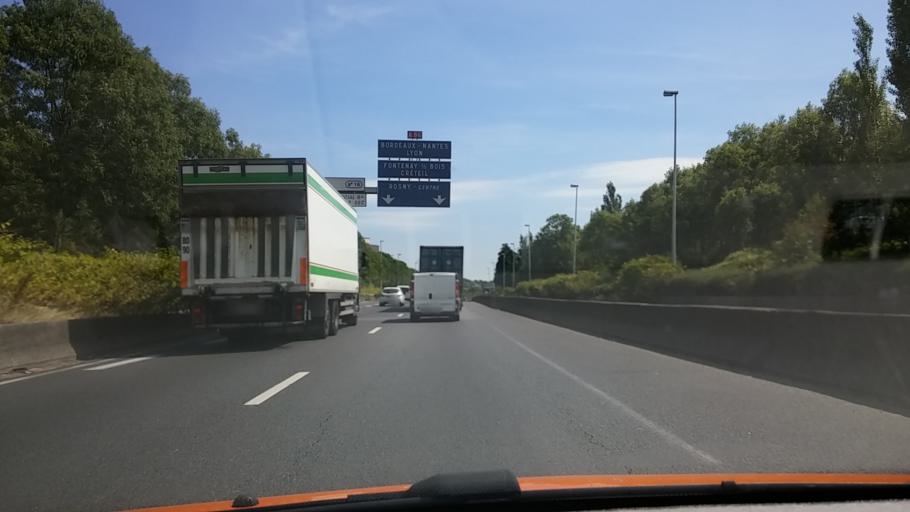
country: FR
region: Ile-de-France
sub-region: Departement de Seine-Saint-Denis
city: Noisy-le-Sec
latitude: 48.8829
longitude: 2.4709
